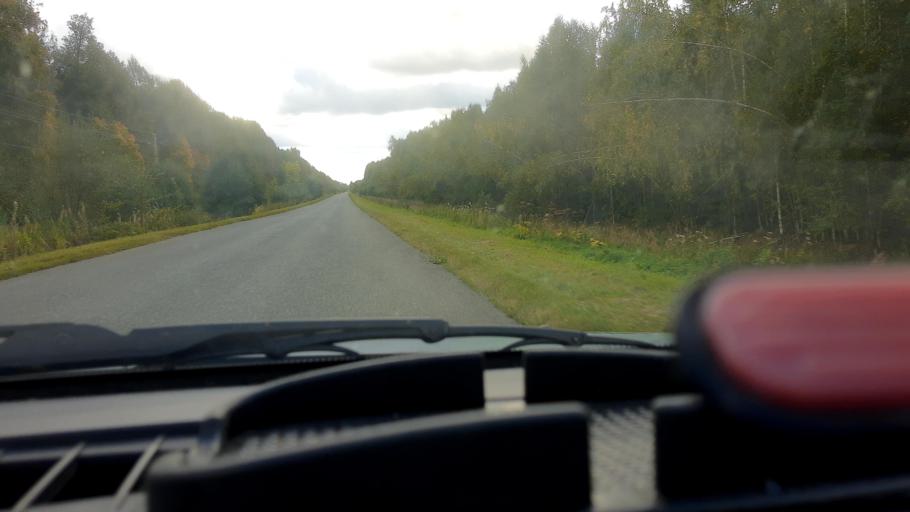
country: RU
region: Mariy-El
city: Kilemary
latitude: 56.9182
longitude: 46.7192
